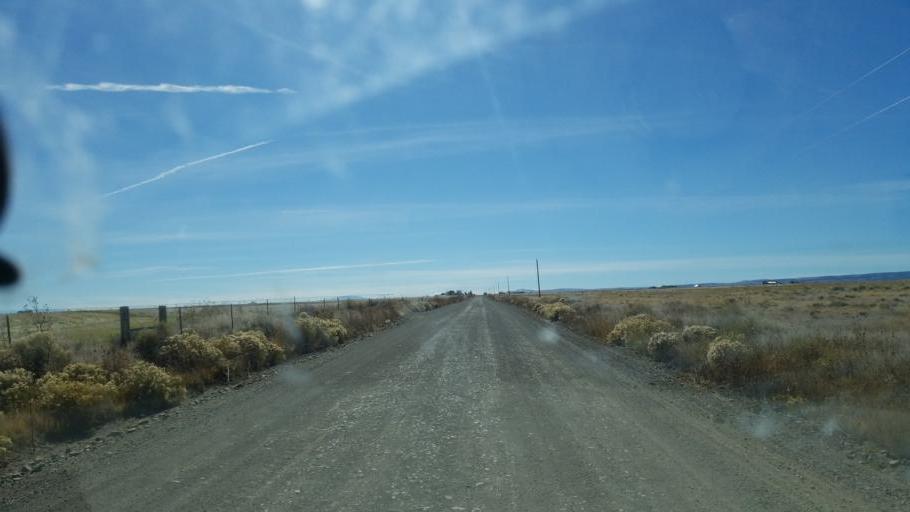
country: US
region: Colorado
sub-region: Rio Grande County
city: Monte Vista
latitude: 37.3954
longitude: -106.1495
